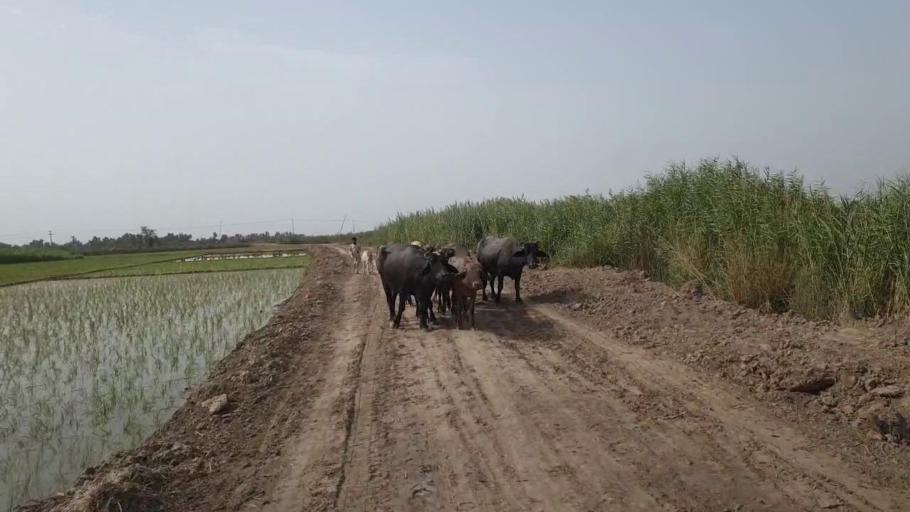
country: PK
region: Sindh
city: Daur
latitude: 26.4162
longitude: 68.1603
